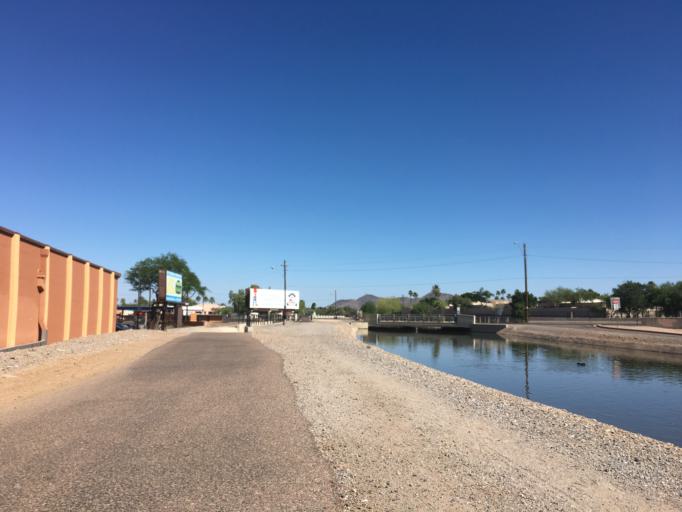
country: US
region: Arizona
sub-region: Maricopa County
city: Phoenix
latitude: 33.5375
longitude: -112.0454
